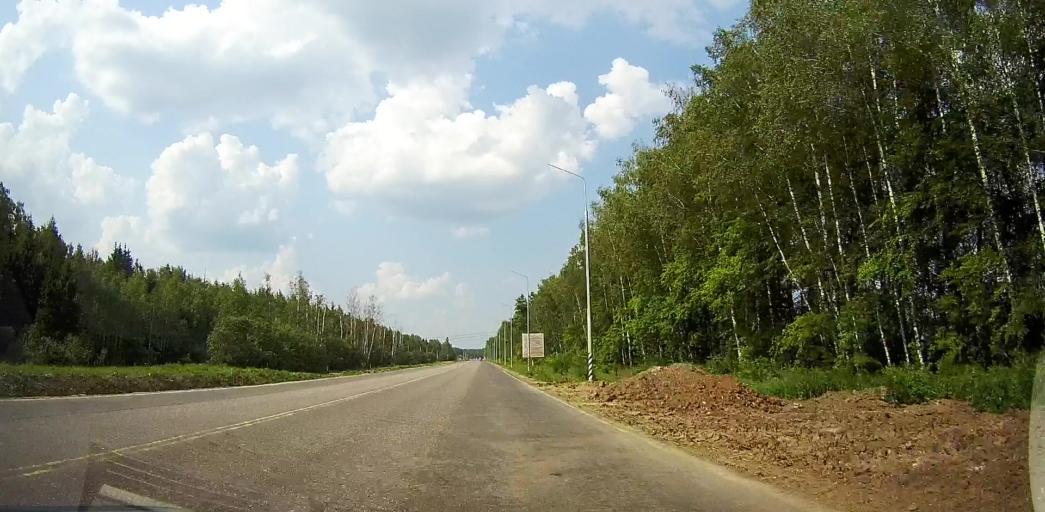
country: RU
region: Moskovskaya
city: Mikhnevo
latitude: 55.0639
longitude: 37.9538
